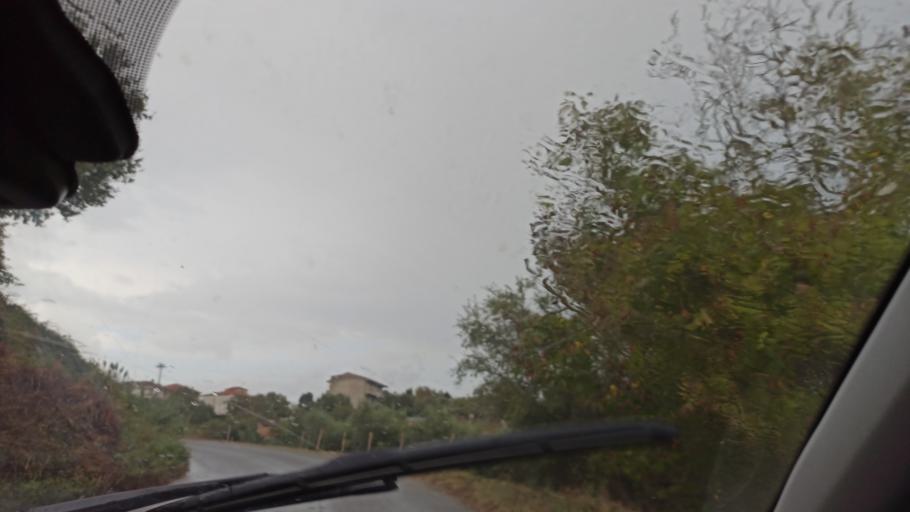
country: IT
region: Calabria
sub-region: Provincia di Vibo-Valentia
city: Paravati
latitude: 38.5836
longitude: 16.0797
